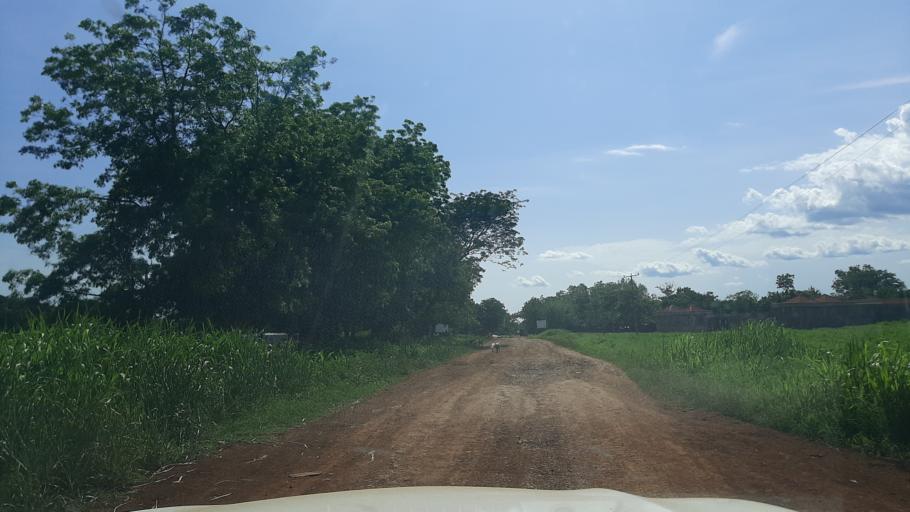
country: ET
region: Gambela
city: Gambela
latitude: 7.8972
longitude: 34.5458
